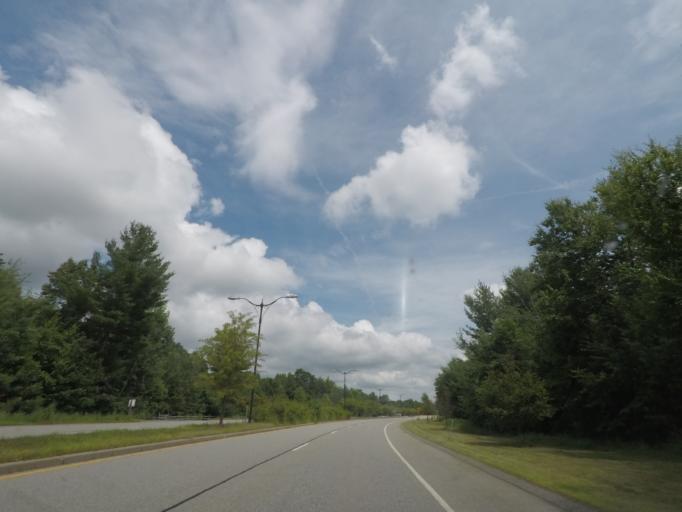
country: US
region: New York
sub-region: Saratoga County
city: Country Knolls
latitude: 42.9563
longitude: -73.7640
